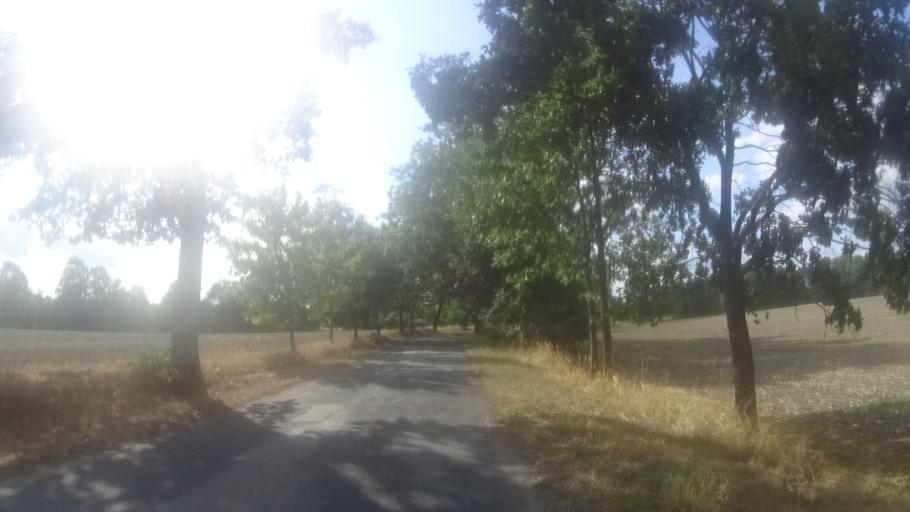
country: CZ
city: Albrechtice nad Orlici
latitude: 50.1541
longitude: 16.0497
